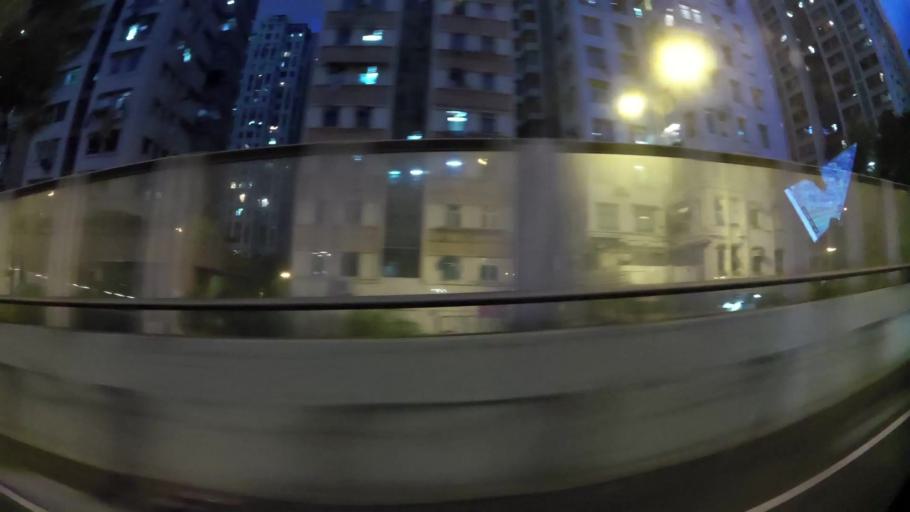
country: HK
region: Kowloon City
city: Kowloon
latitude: 22.3141
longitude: 114.1670
